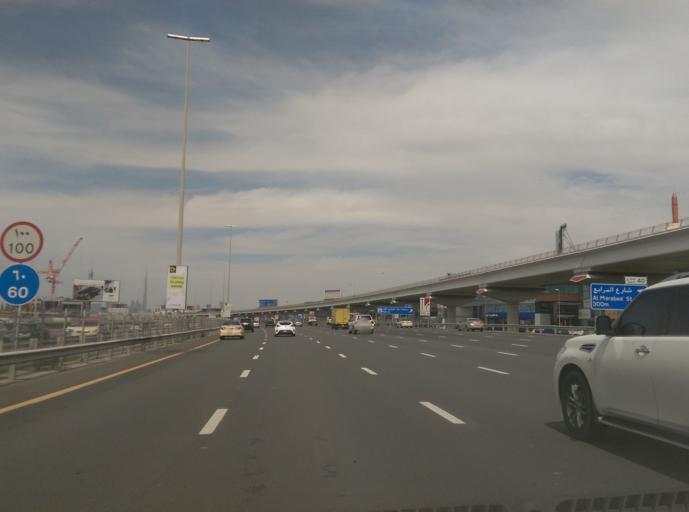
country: AE
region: Dubai
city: Dubai
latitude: 25.1275
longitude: 55.2084
